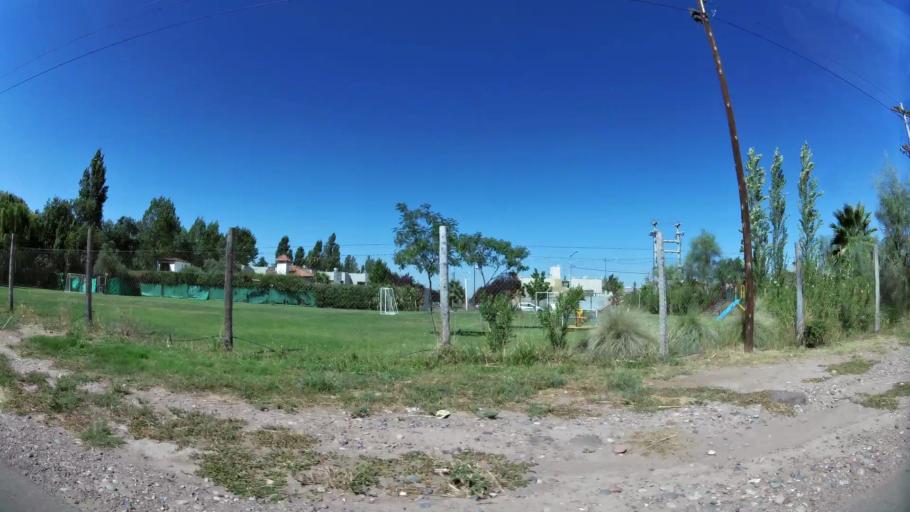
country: AR
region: Mendoza
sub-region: Departamento de Godoy Cruz
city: Godoy Cruz
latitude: -32.9809
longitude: -68.8427
